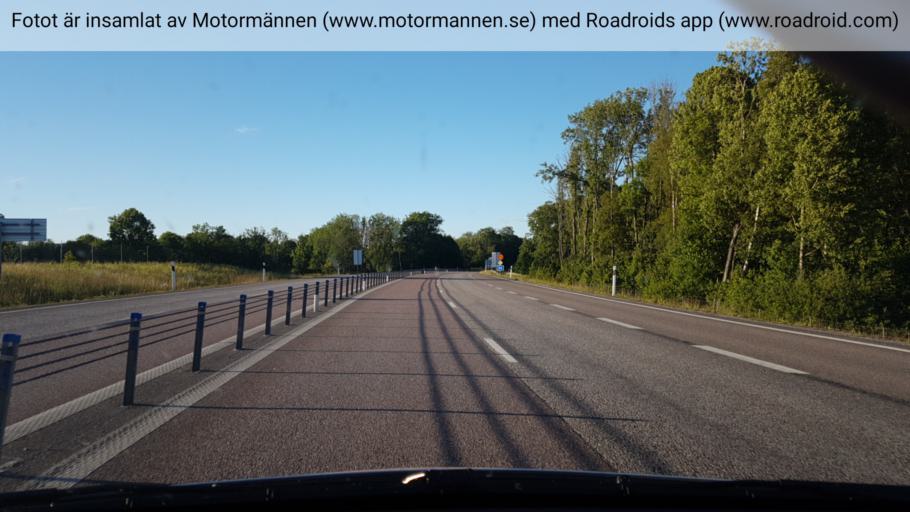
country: SE
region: Vaestra Goetaland
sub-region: Skovde Kommun
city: Skultorp
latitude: 58.3119
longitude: 13.8103
